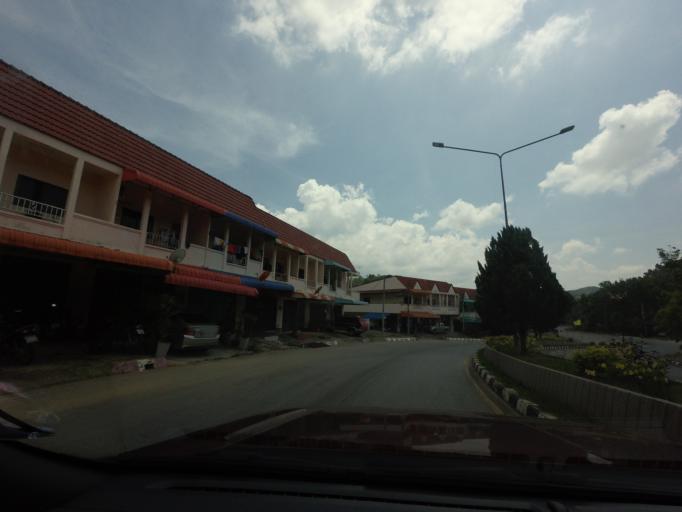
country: TH
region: Yala
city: Betong
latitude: 5.7719
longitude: 101.0596
